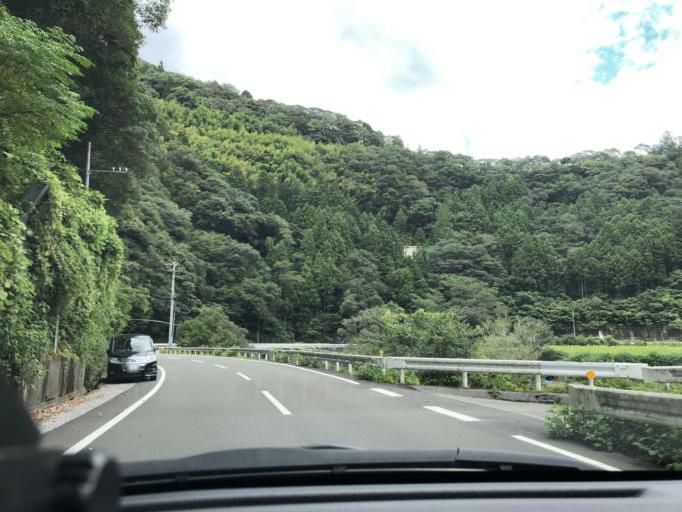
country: JP
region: Kochi
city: Kochi-shi
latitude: 33.6348
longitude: 133.5201
